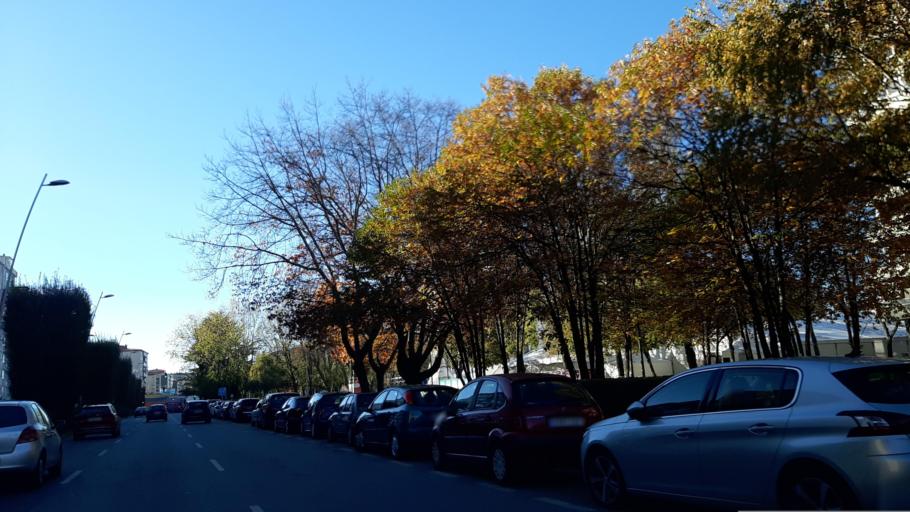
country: ES
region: Galicia
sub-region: Provincia de Pontevedra
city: Vigo
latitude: 42.2191
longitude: -8.7405
